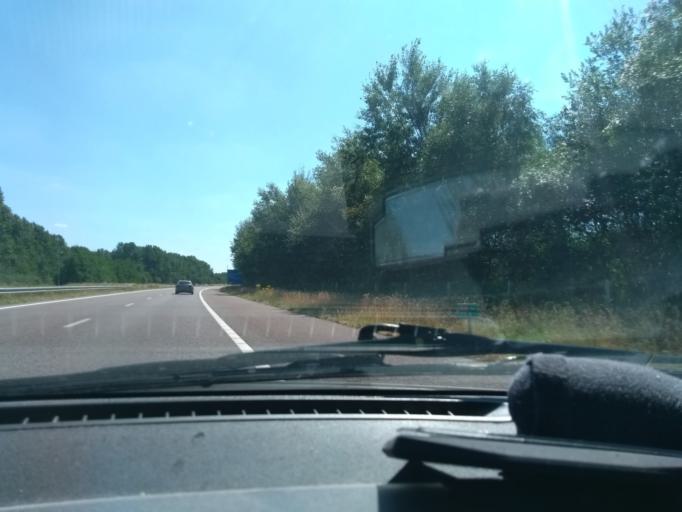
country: NL
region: Drenthe
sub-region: Gemeente Emmen
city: Klazienaveen
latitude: 52.7328
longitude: 7.0266
